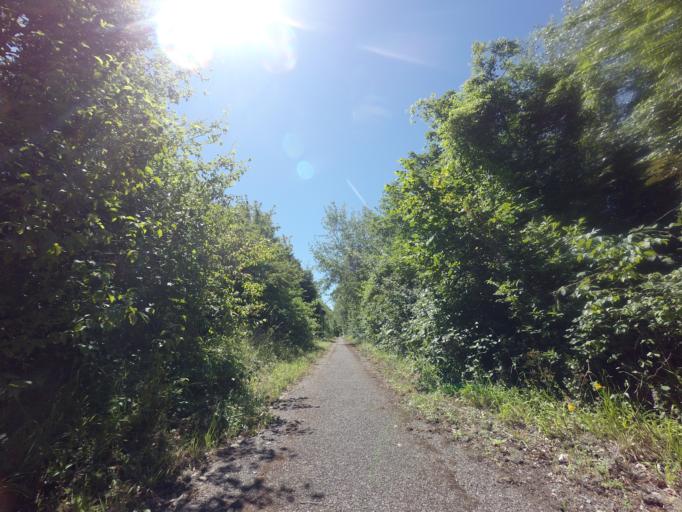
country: GB
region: England
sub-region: Kent
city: Eastry
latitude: 51.2238
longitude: 1.3010
